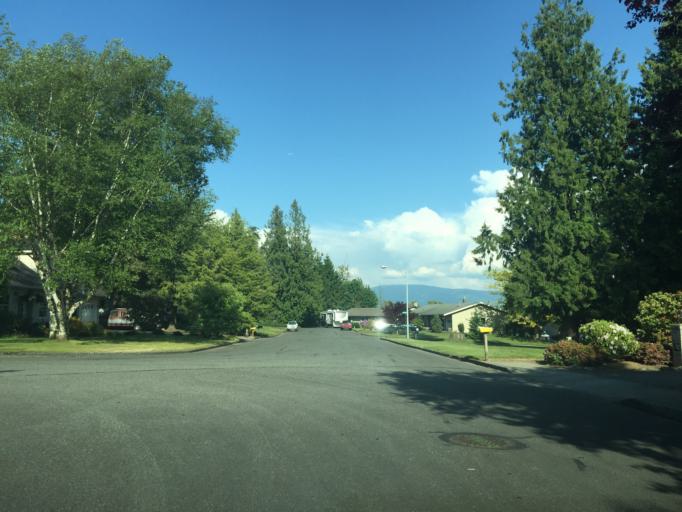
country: US
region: Washington
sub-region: Whatcom County
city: Lynden
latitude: 48.9347
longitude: -122.4751
